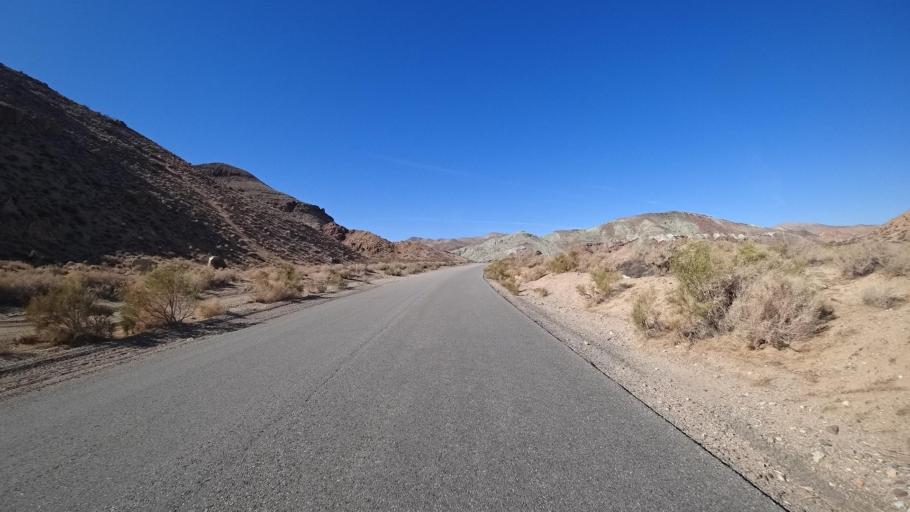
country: US
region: California
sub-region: Kern County
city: California City
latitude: 35.3161
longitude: -118.0742
